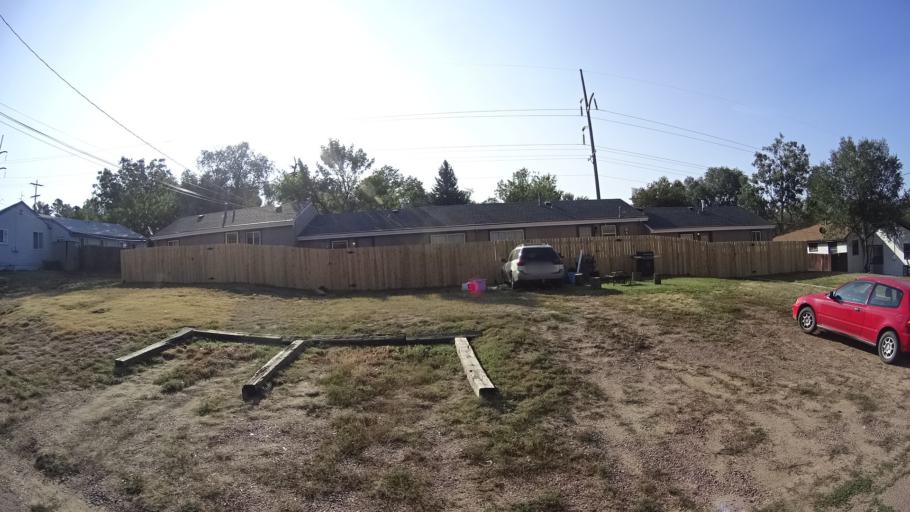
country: US
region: Colorado
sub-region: El Paso County
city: Colorado Springs
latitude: 38.8542
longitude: -104.8637
